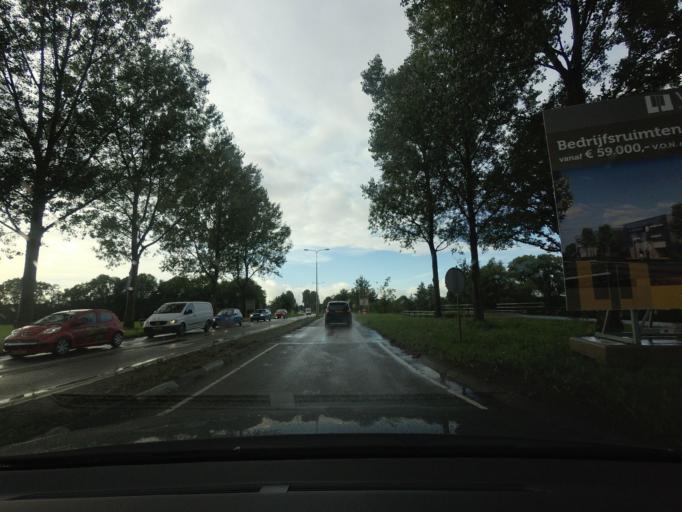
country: NL
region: South Holland
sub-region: Gemeente Voorschoten
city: Voorschoten
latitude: 52.1286
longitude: 4.4309
